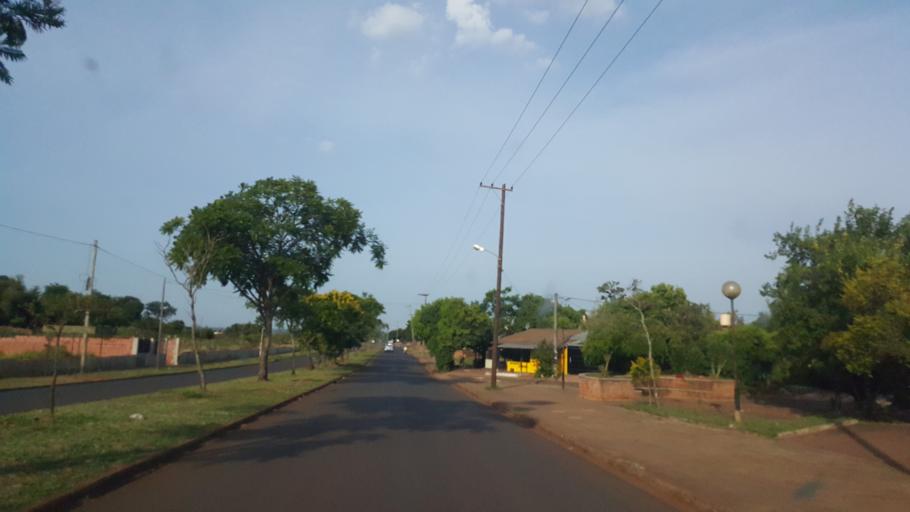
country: AR
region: Misiones
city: Garupa
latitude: -27.4368
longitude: -55.8808
